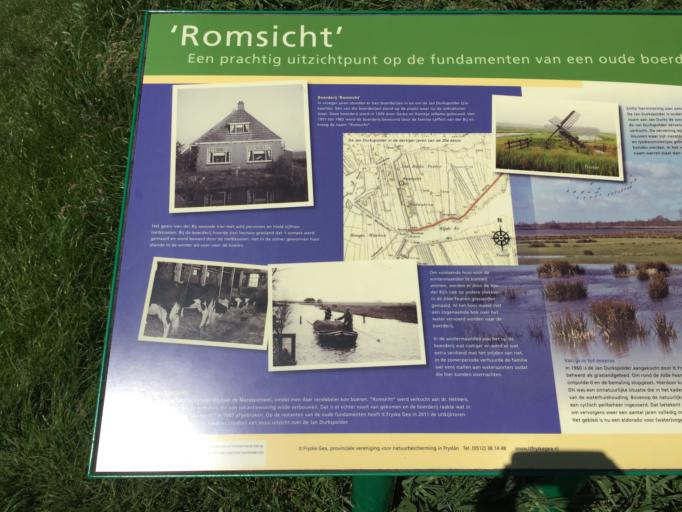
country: NL
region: Friesland
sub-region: Gemeente Smallingerland
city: Oudega
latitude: 53.1147
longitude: 5.9473
